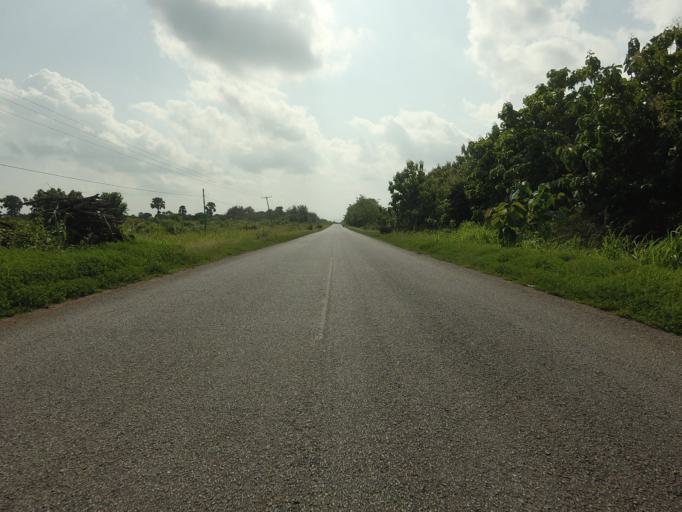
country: GH
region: Volta
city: Ho
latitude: 6.5787
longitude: 0.5825
